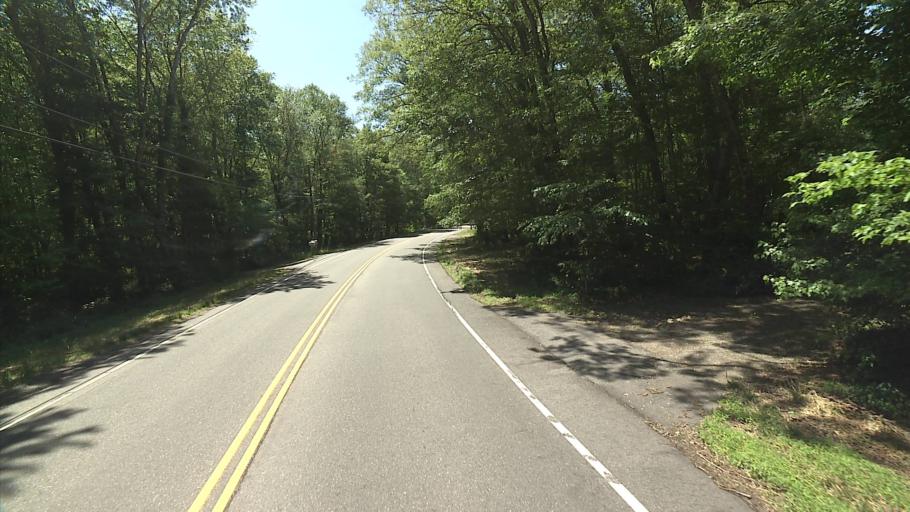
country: US
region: Rhode Island
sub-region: Washington County
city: Hopkinton
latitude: 41.4981
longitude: -71.8315
